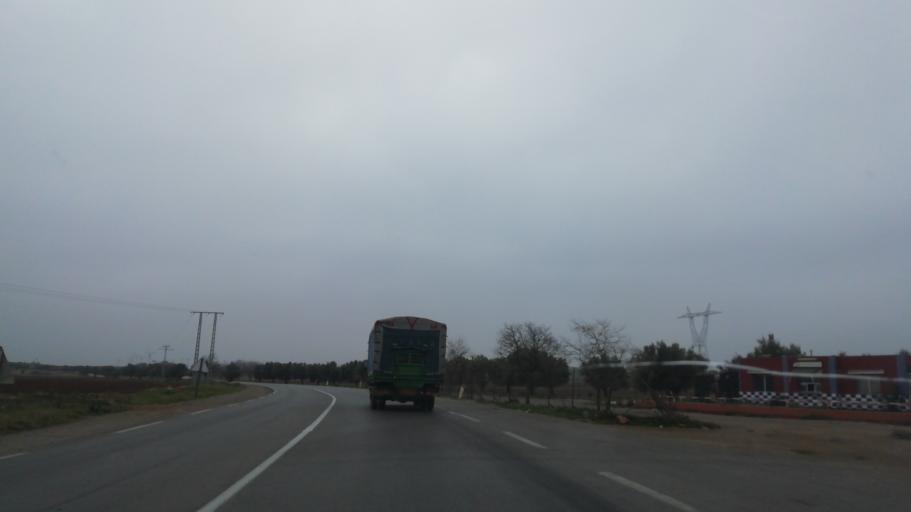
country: DZ
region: Mascara
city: Mascara
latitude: 35.3187
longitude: 0.3690
